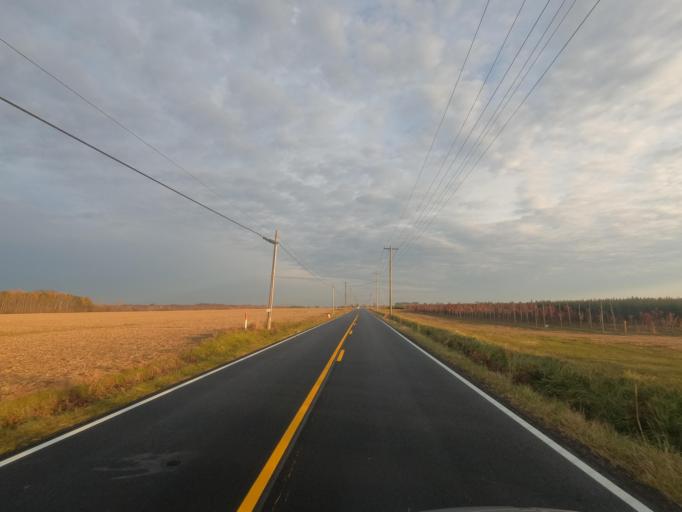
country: US
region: Delaware
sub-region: New Castle County
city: Townsend
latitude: 39.2813
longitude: -75.8374
